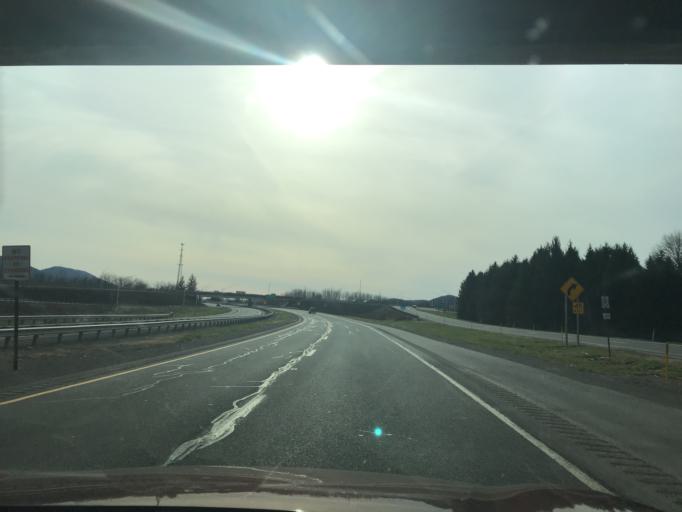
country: US
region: Pennsylvania
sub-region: Lycoming County
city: Duboistown
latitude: 41.2318
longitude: -77.0367
